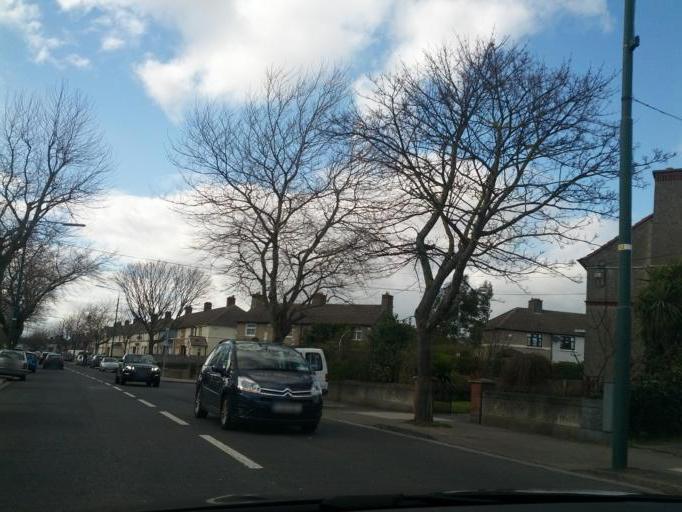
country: IE
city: Donnycarney
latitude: 53.3735
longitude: -6.2111
